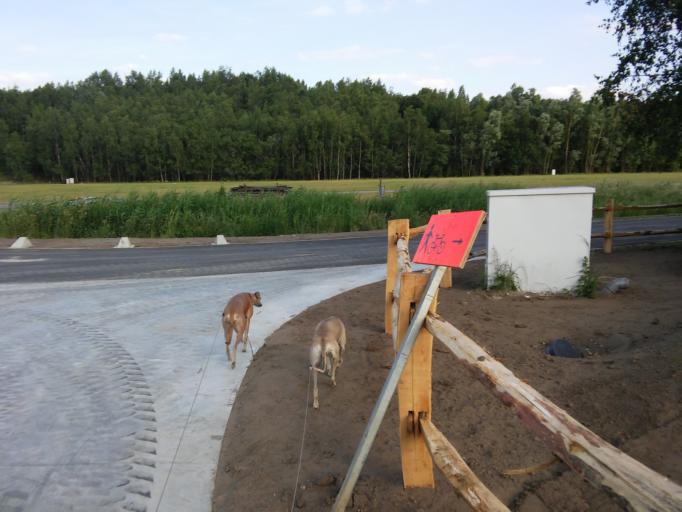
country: BE
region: Flanders
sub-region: Provincie Antwerpen
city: Boom
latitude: 51.0912
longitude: 4.3839
